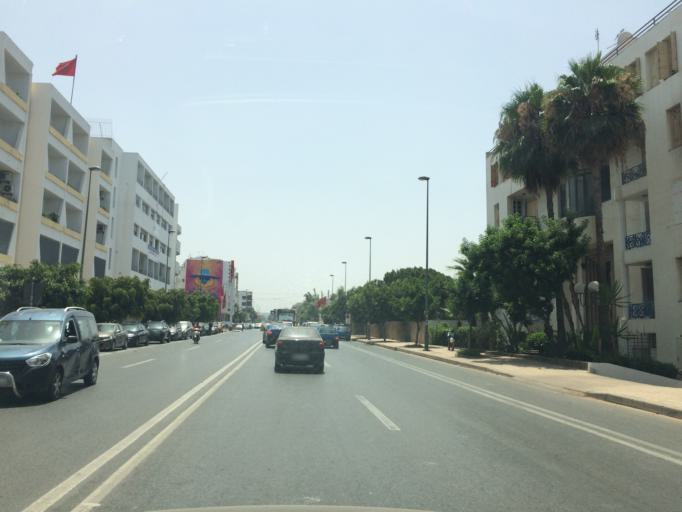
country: MA
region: Rabat-Sale-Zemmour-Zaer
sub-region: Rabat
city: Rabat
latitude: 33.9976
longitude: -6.8512
